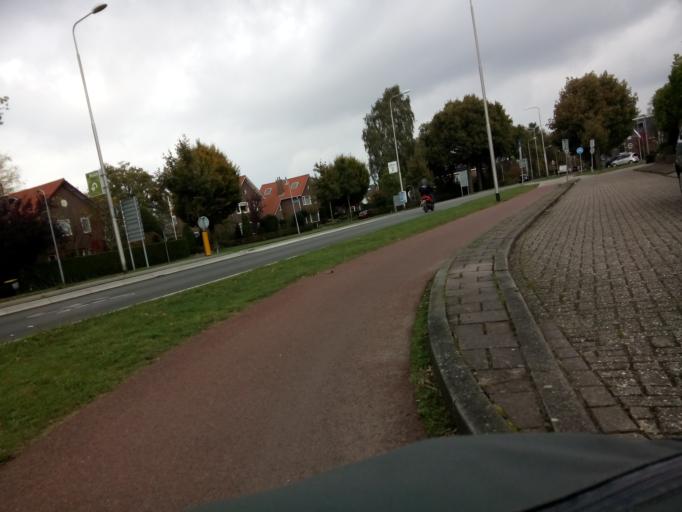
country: NL
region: Gelderland
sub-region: Gemeente Ermelo
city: Ermelo
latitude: 52.2935
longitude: 5.6292
